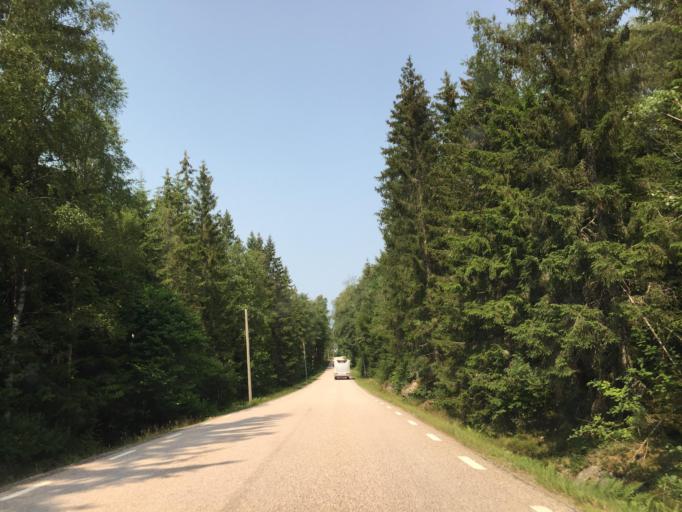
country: SE
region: Vaestra Goetaland
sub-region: Lilla Edets Kommun
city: Lilla Edet
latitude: 58.1378
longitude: 12.0092
